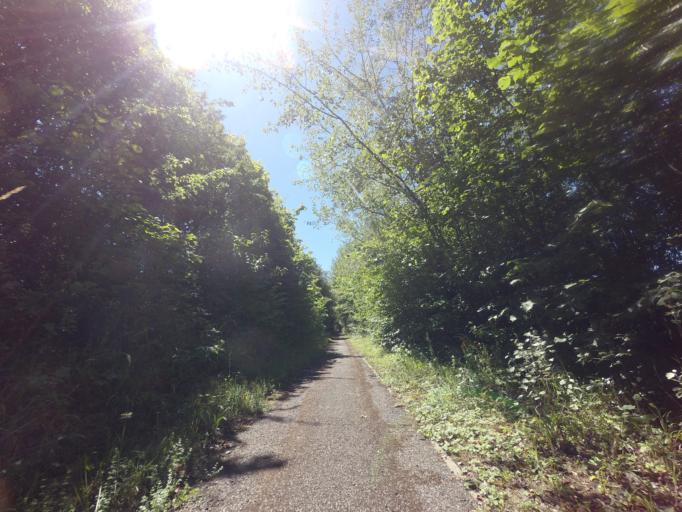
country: GB
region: England
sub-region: Kent
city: Eastry
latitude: 51.2232
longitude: 1.3010
